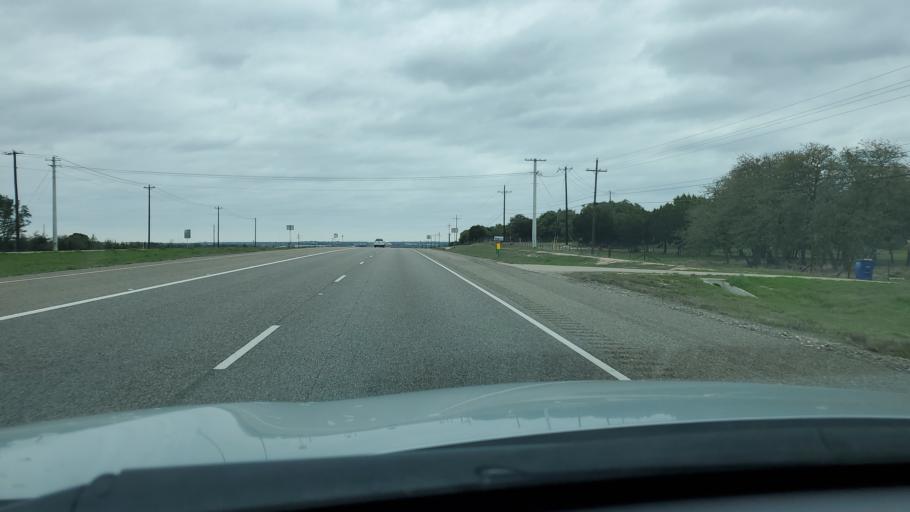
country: US
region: Texas
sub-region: Williamson County
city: Florence
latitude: 30.8058
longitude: -97.7704
